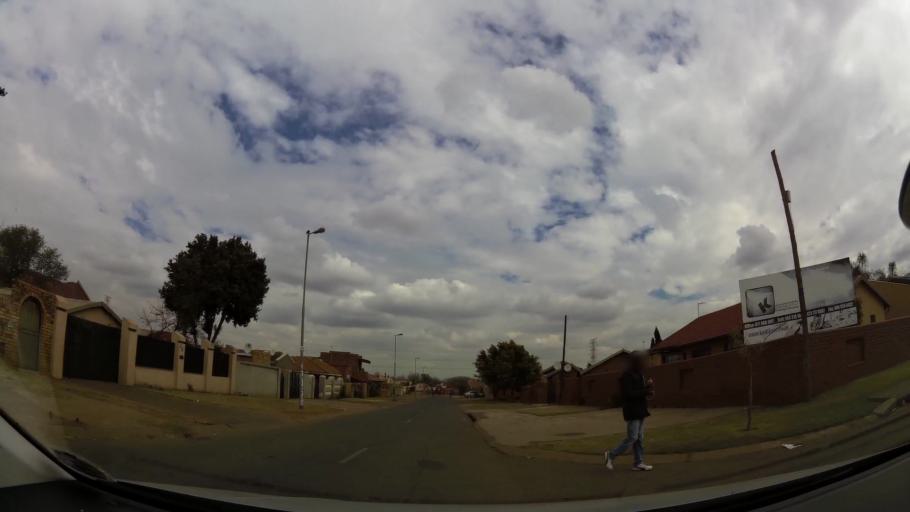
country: ZA
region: Gauteng
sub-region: City of Johannesburg Metropolitan Municipality
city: Soweto
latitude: -26.2834
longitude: 27.8515
